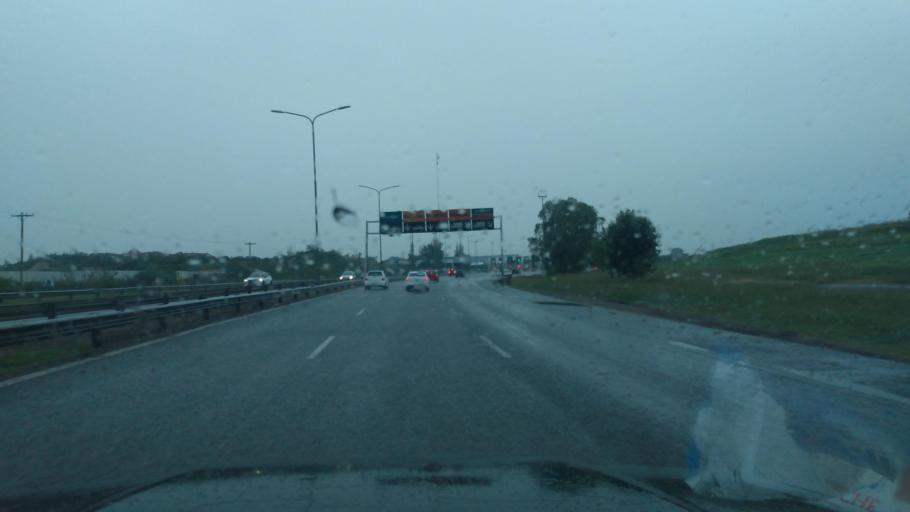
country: AR
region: Buenos Aires
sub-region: Partido de Tigre
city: Tigre
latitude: -34.5005
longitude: -58.5900
